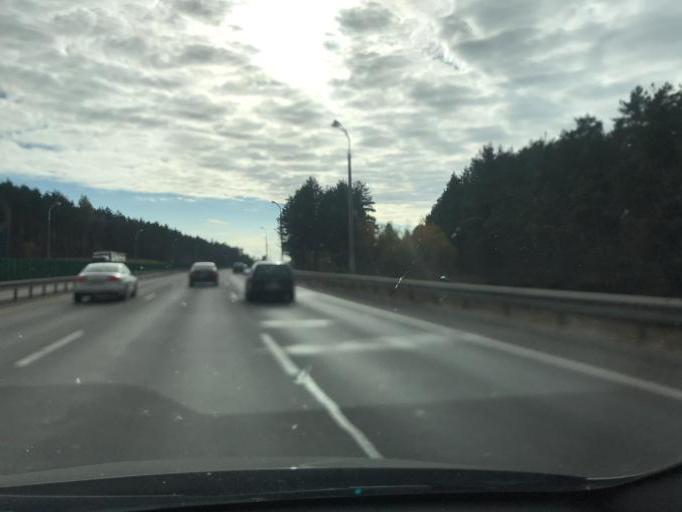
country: BY
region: Minsk
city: Vyaliki Trastsyanets
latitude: 53.8799
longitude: 27.6966
